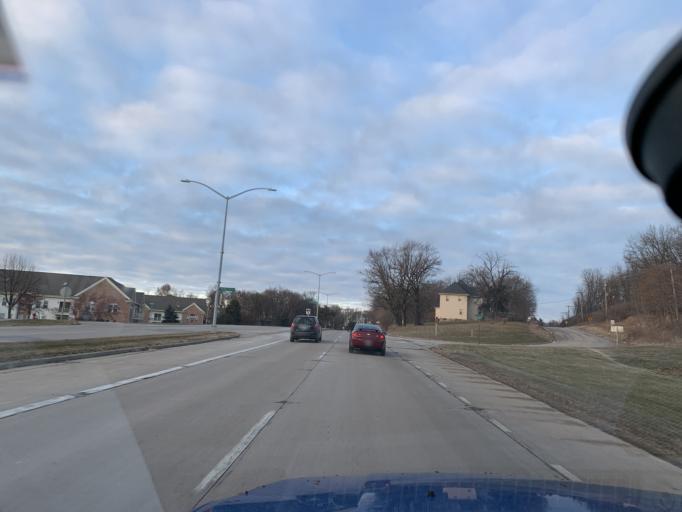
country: US
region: Wisconsin
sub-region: Dane County
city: Fitchburg
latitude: 43.0074
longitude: -89.4278
